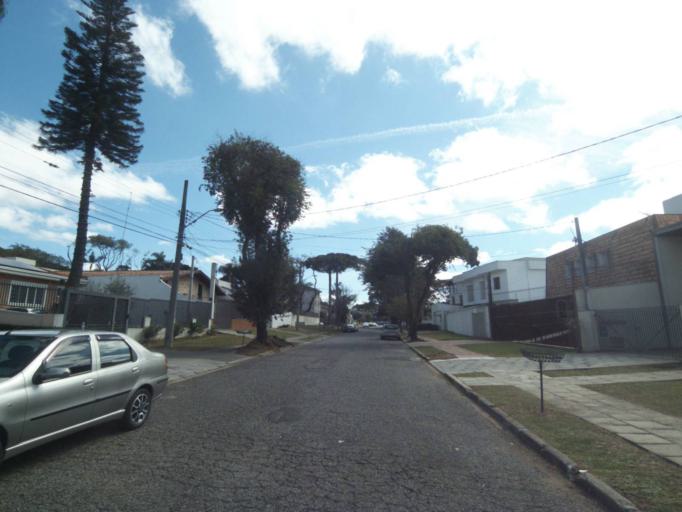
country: BR
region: Parana
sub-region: Curitiba
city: Curitiba
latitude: -25.4542
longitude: -49.2729
